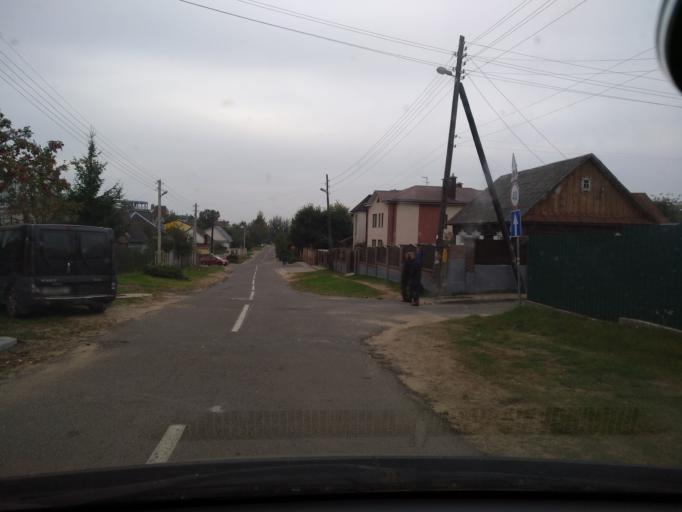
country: BY
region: Minsk
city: Minsk
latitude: 53.9420
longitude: 27.5832
